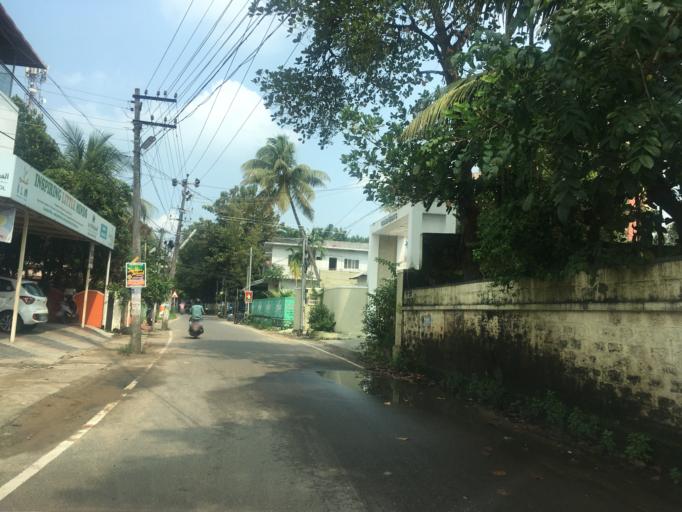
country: IN
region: Kerala
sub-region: Ernakulam
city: Elur
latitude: 10.0398
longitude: 76.3061
